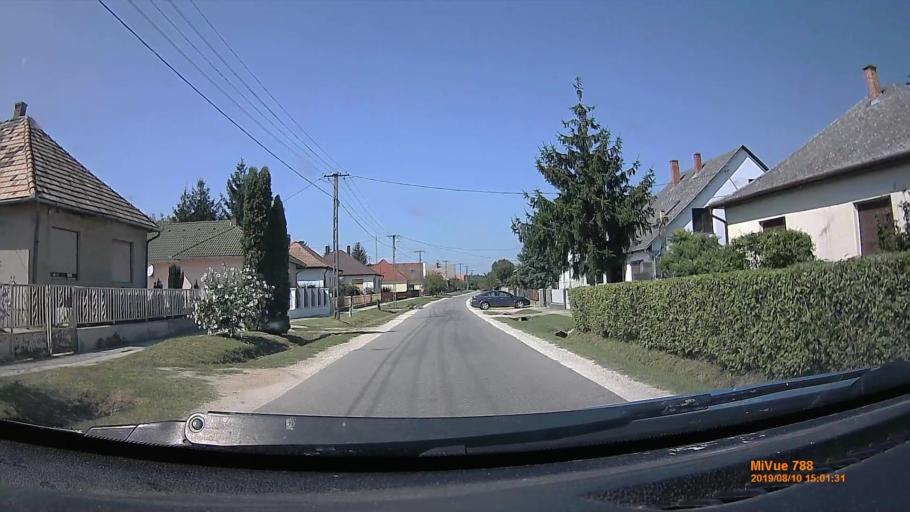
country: HU
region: Somogy
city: Lengyeltoti
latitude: 46.6499
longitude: 17.5771
